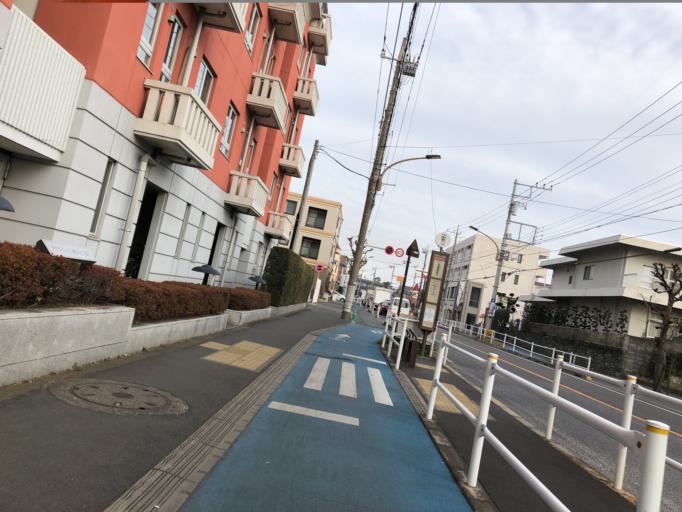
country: JP
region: Tokyo
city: Mitaka-shi
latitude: 35.6887
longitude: 139.5456
